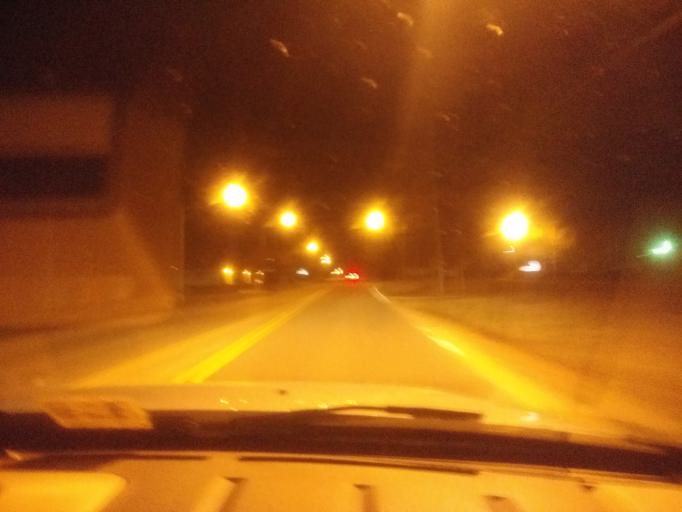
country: US
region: Virginia
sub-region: City of Chesapeake
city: Chesapeake
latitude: 36.7902
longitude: -76.1965
